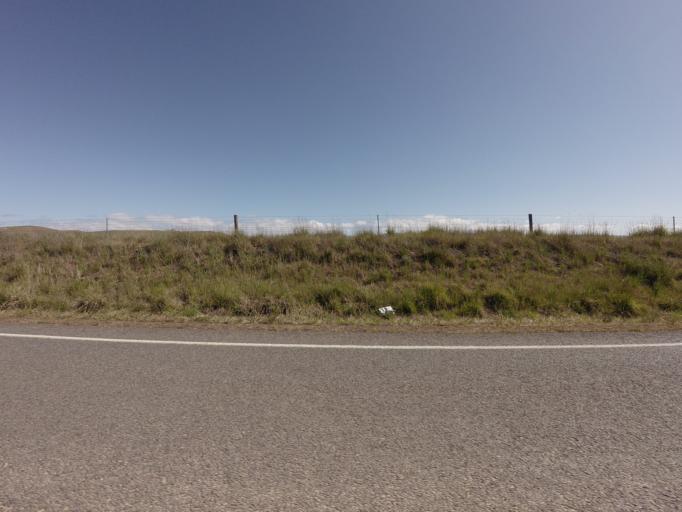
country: AU
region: Tasmania
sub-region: Derwent Valley
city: New Norfolk
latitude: -42.5431
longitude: 146.7746
